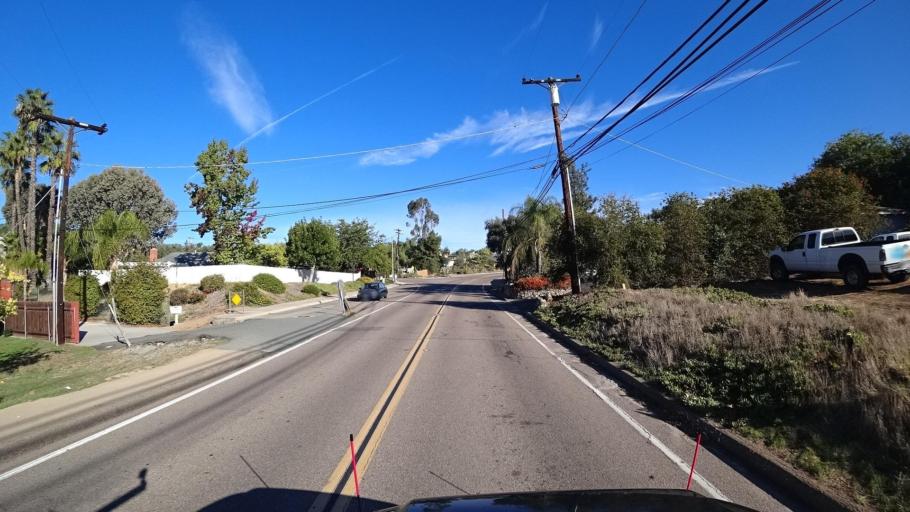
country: US
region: California
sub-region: San Diego County
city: Lakeside
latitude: 32.8468
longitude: -116.9052
